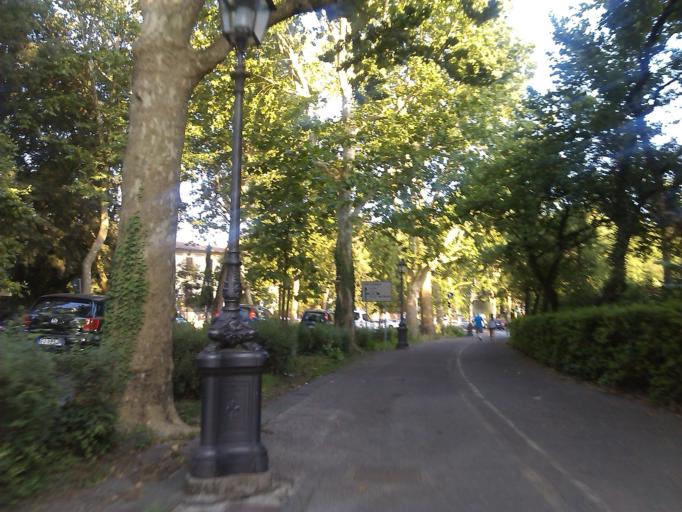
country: IT
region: Tuscany
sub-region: Province of Florence
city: Florence
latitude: 43.7628
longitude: 11.2721
